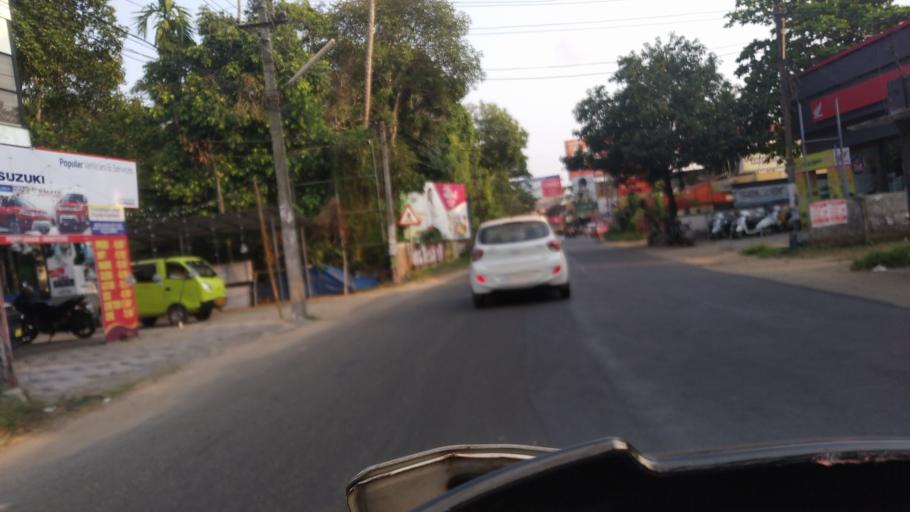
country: IN
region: Kerala
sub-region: Thrissur District
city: Irinjalakuda
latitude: 10.3169
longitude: 76.1466
